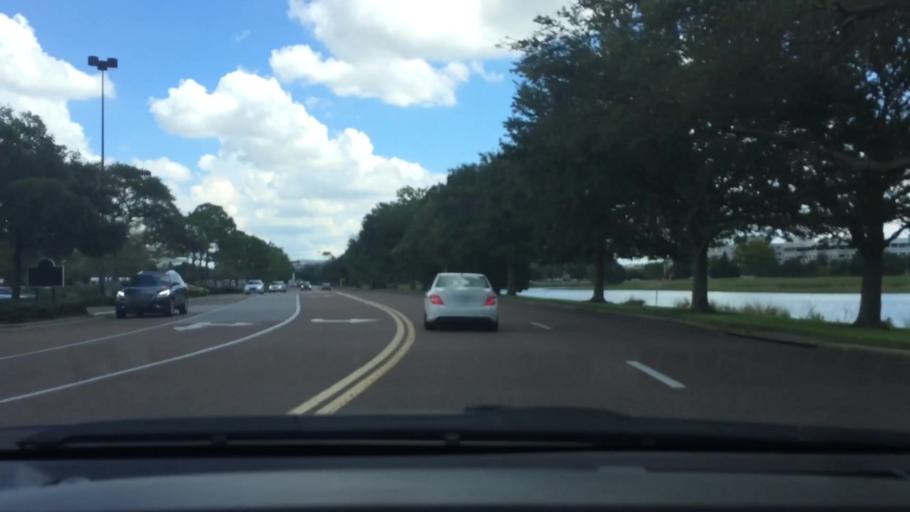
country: US
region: Florida
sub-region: Hillsborough County
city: Egypt Lake-Leto
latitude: 27.9621
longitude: -82.5230
